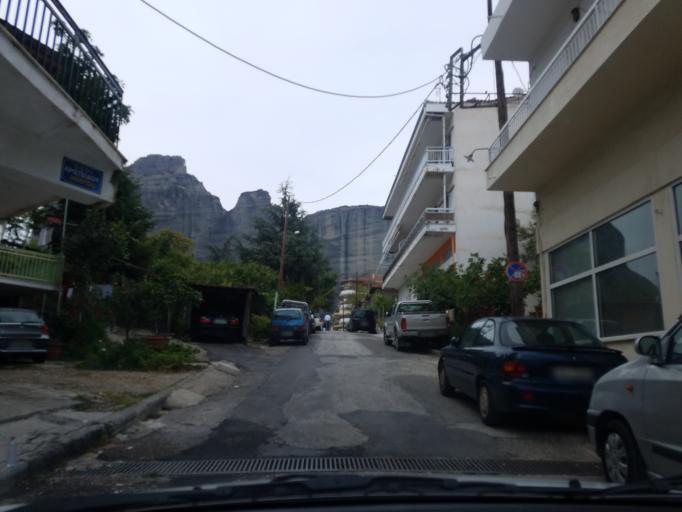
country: GR
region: Thessaly
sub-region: Trikala
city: Kalampaka
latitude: 39.7037
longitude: 21.6300
